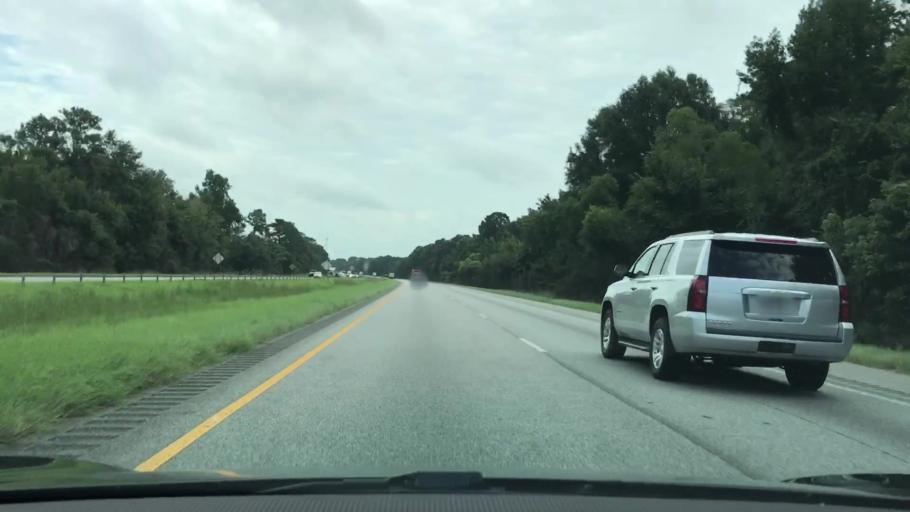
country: US
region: Alabama
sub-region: Montgomery County
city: Pike Road
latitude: 32.3826
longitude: -86.0046
